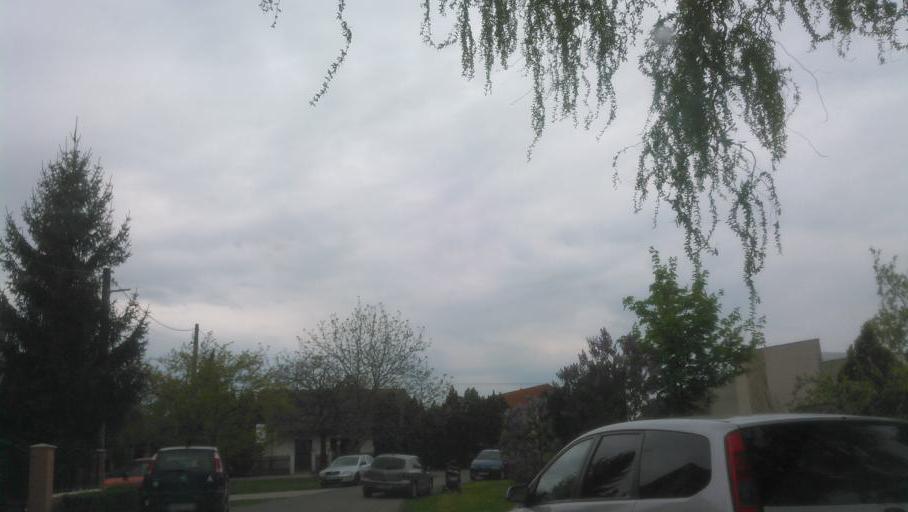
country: SK
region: Bratislavsky
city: Senec
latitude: 48.1472
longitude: 17.3389
